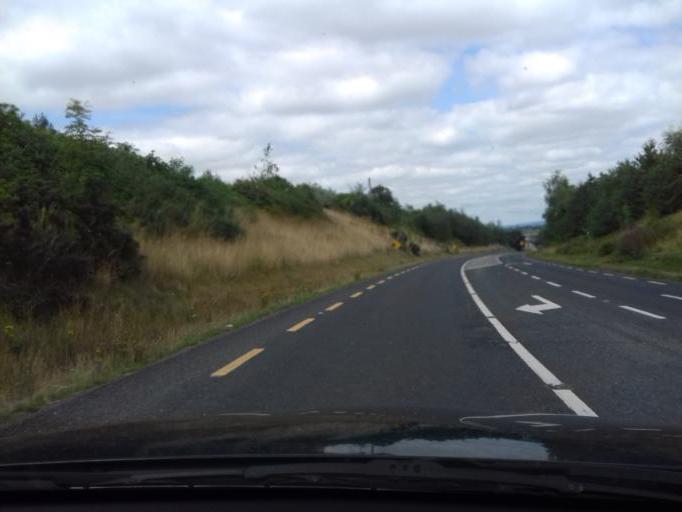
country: IE
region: Leinster
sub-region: County Carlow
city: Tullow
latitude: 52.7891
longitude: -6.7540
